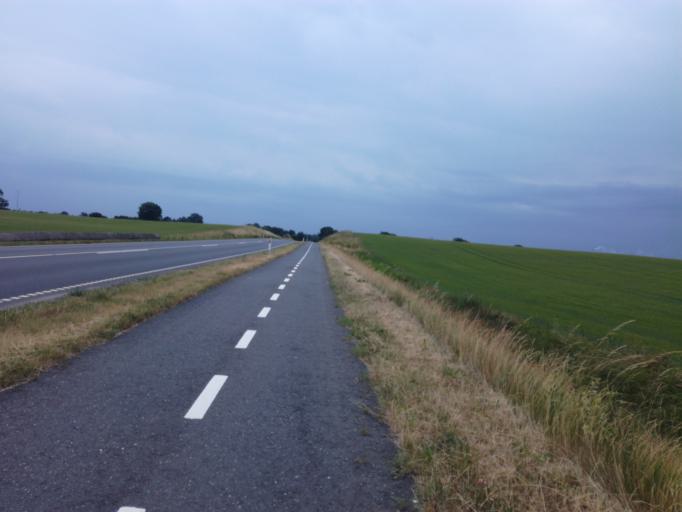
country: DK
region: South Denmark
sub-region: Vejle Kommune
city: Borkop
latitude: 55.6717
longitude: 9.6178
